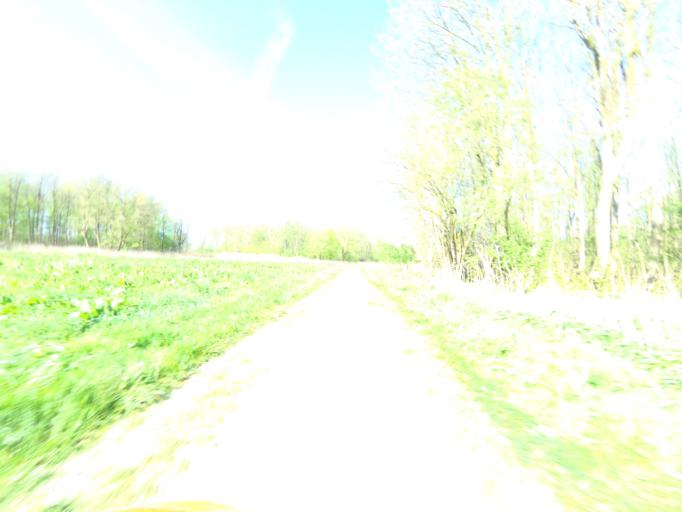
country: NL
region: Flevoland
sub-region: Gemeente Lelystad
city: Lelystad
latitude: 52.4463
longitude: 5.5578
